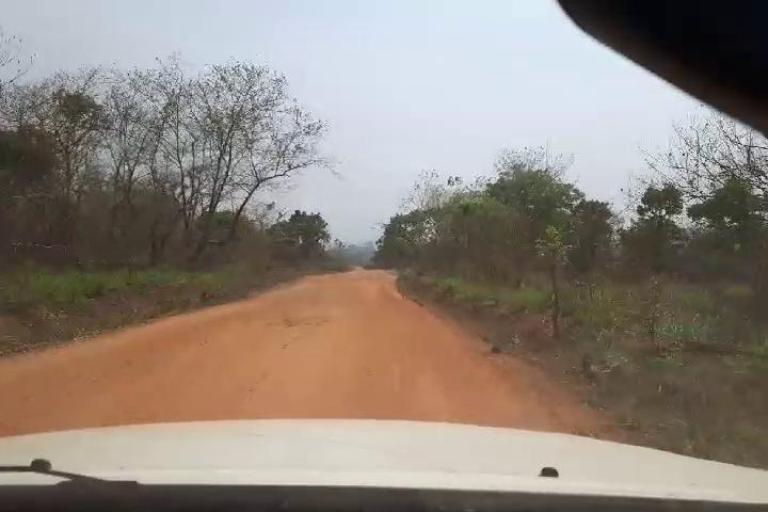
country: SL
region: Northern Province
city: Bumbuna
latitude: 8.9582
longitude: -11.8037
